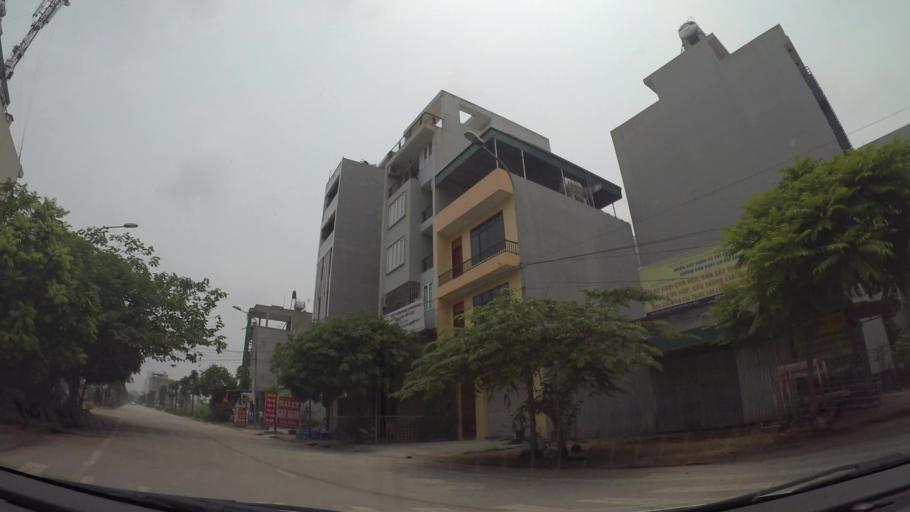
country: VN
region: Ha Noi
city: Ha Dong
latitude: 20.9753
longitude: 105.7667
